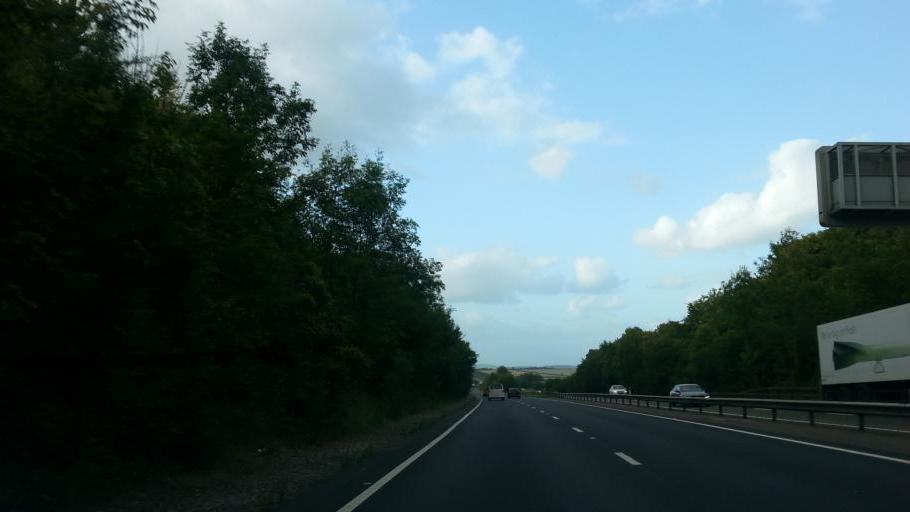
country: GB
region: England
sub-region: Hampshire
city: Overton
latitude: 51.1860
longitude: -1.3365
